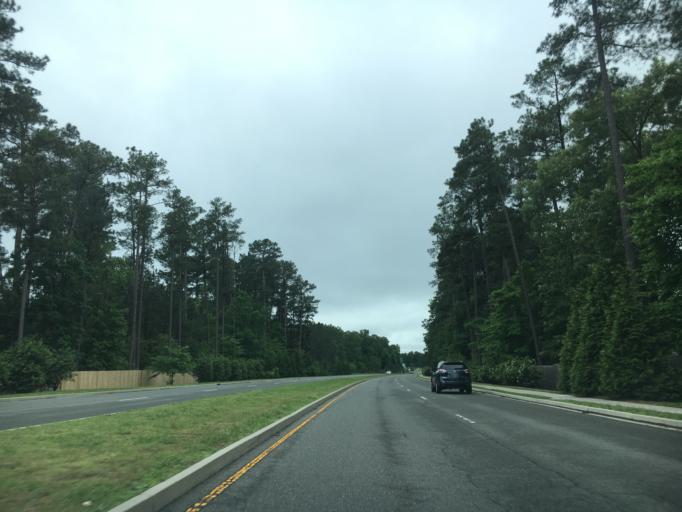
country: US
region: Virginia
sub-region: Henrico County
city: Short Pump
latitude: 37.6264
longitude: -77.6169
